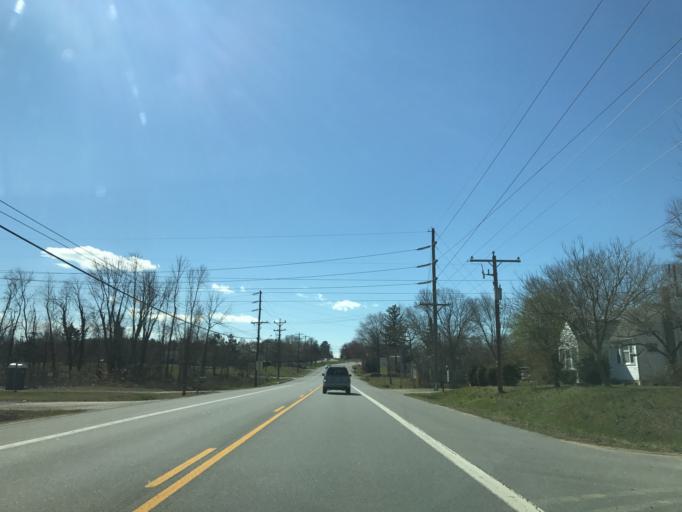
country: US
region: Maryland
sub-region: Kent County
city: Chestertown
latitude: 39.2260
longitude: -76.0590
